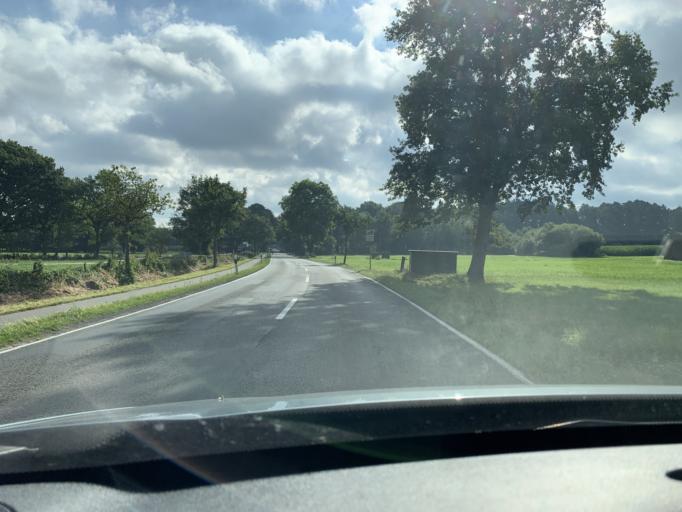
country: DE
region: Lower Saxony
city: Wardenburg
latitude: 53.0720
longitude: 8.1508
